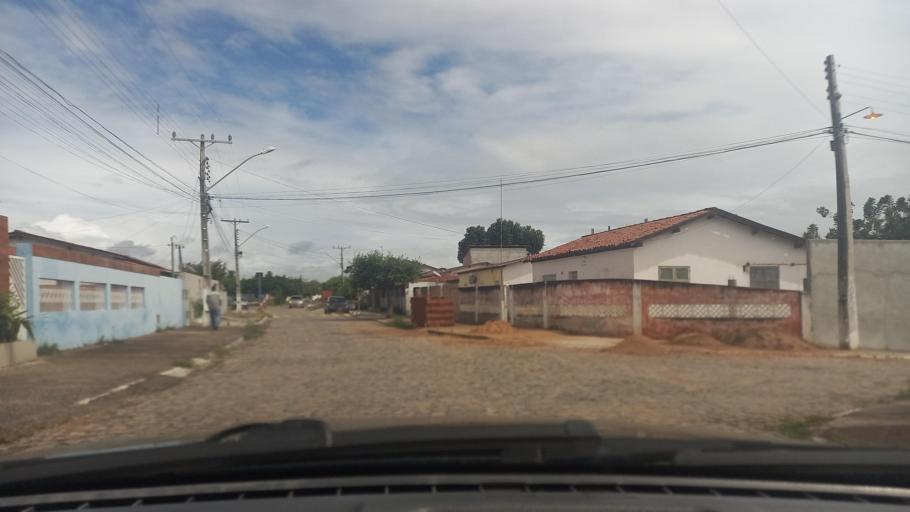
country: BR
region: Bahia
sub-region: Paulo Afonso
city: Paulo Afonso
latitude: -9.3398
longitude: -38.2568
